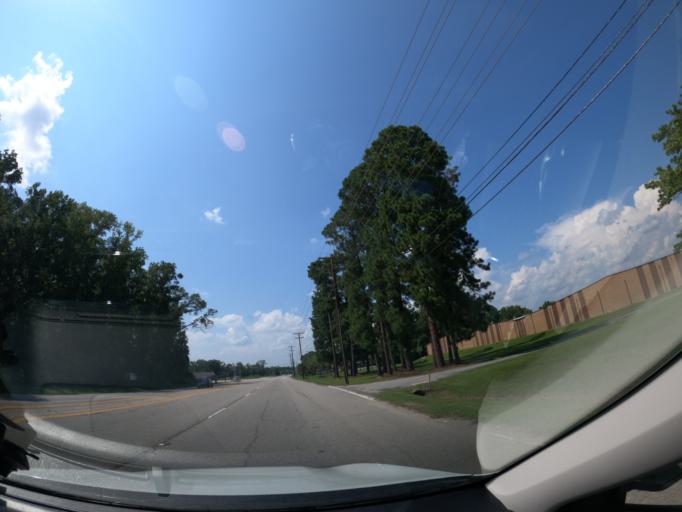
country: US
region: South Carolina
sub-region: Richland County
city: Columbia
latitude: 33.9442
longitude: -80.9864
